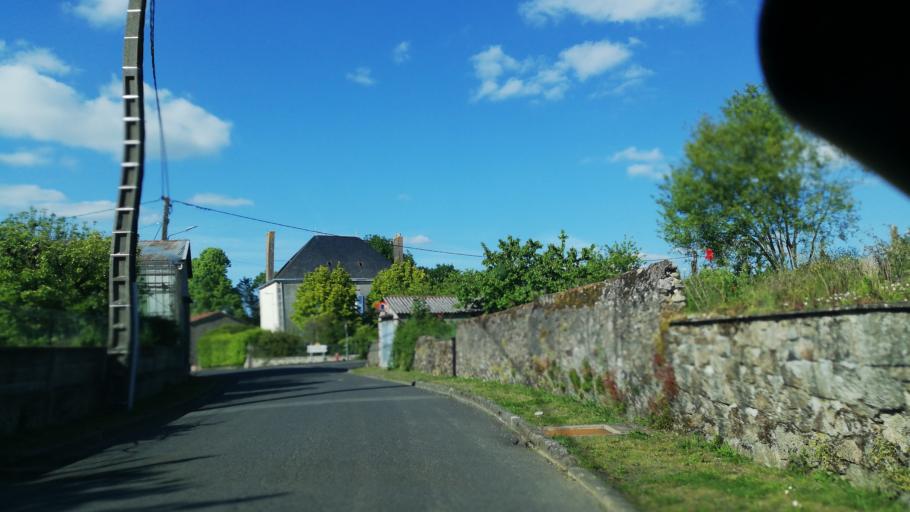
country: FR
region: Poitou-Charentes
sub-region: Departement des Deux-Sevres
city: Moncoutant
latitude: 46.6837
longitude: -0.5747
